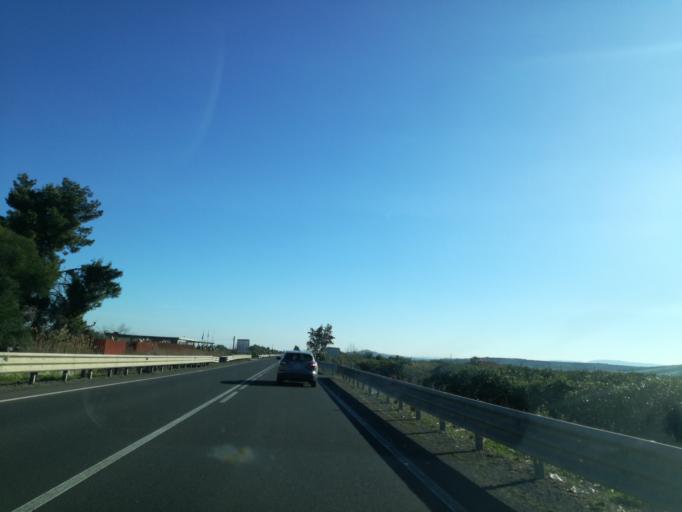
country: IT
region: Sicily
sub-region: Catania
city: Palagonia
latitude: 37.3815
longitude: 14.7582
